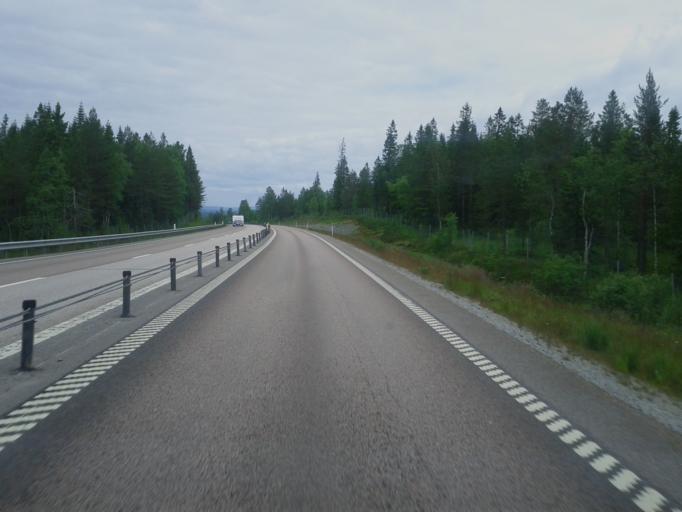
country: SE
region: Vaesternorrland
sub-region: OErnskoeldsviks Kommun
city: Bjasta
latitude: 63.1215
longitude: 18.3977
